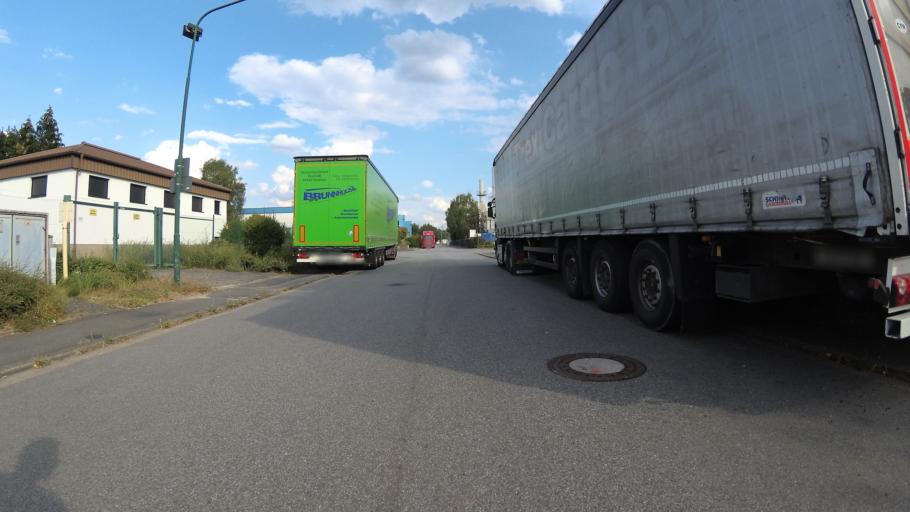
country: DE
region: Saarland
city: Bexbach
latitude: 49.3446
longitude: 7.2309
